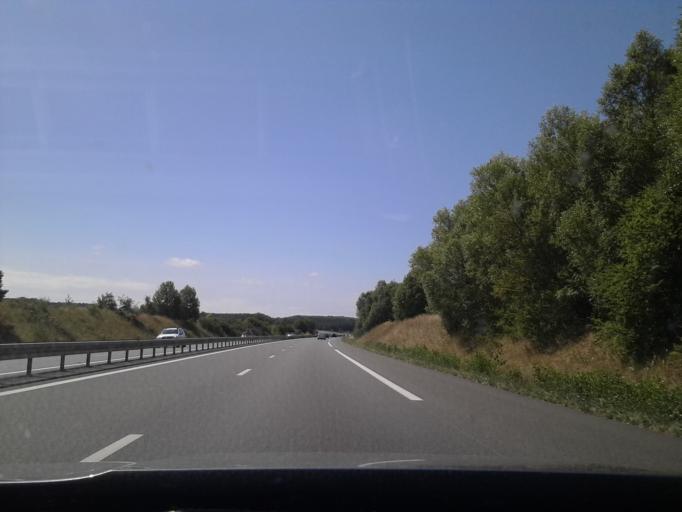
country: FR
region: Pays de la Loire
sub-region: Departement de la Sarthe
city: Teloche
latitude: 47.8694
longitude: 0.3025
